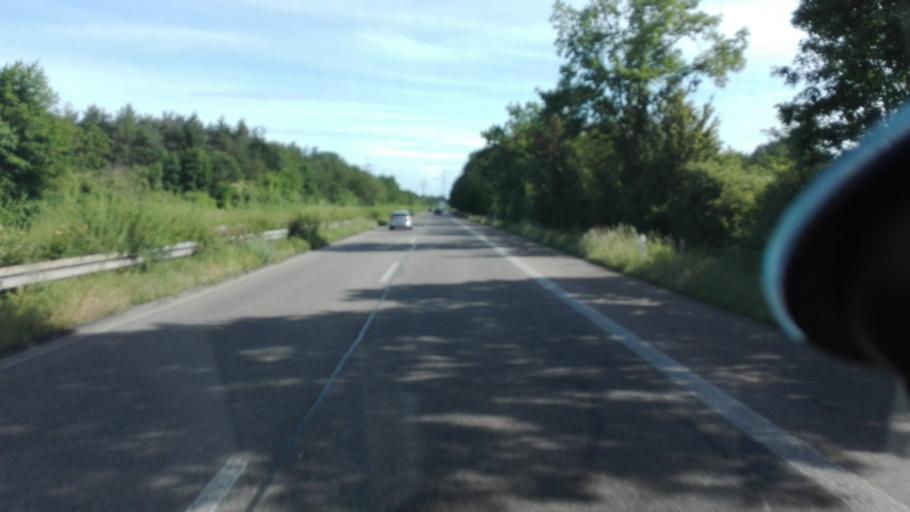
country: DE
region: Baden-Wuerttemberg
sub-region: Karlsruhe Region
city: Eggenstein-Leopoldshafen
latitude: 49.0781
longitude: 8.4079
